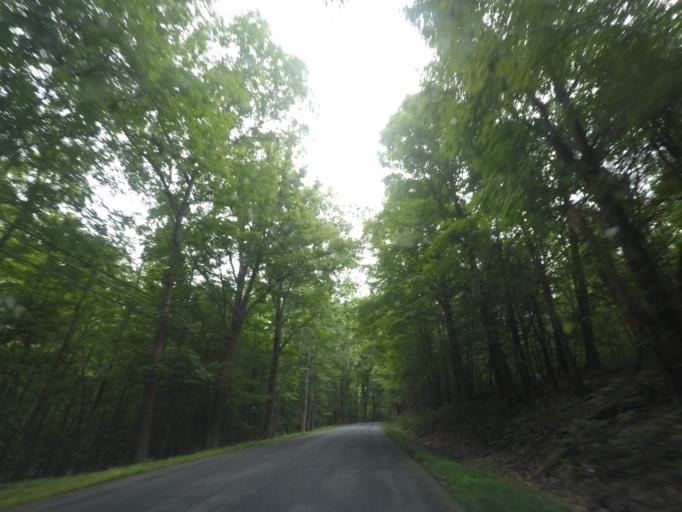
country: US
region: New York
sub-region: Rensselaer County
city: Nassau
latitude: 42.5029
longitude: -73.6061
